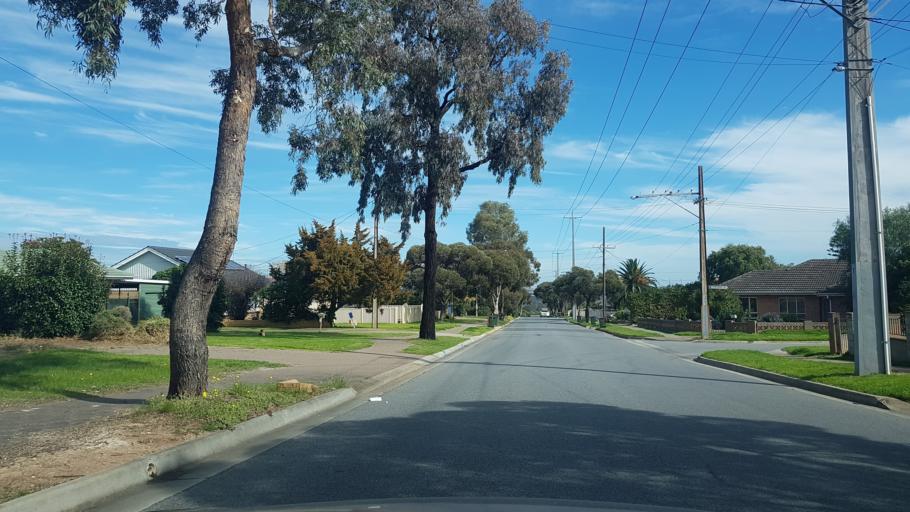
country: AU
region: South Australia
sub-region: Salisbury
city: Ingle Farm
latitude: -34.8193
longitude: 138.6568
